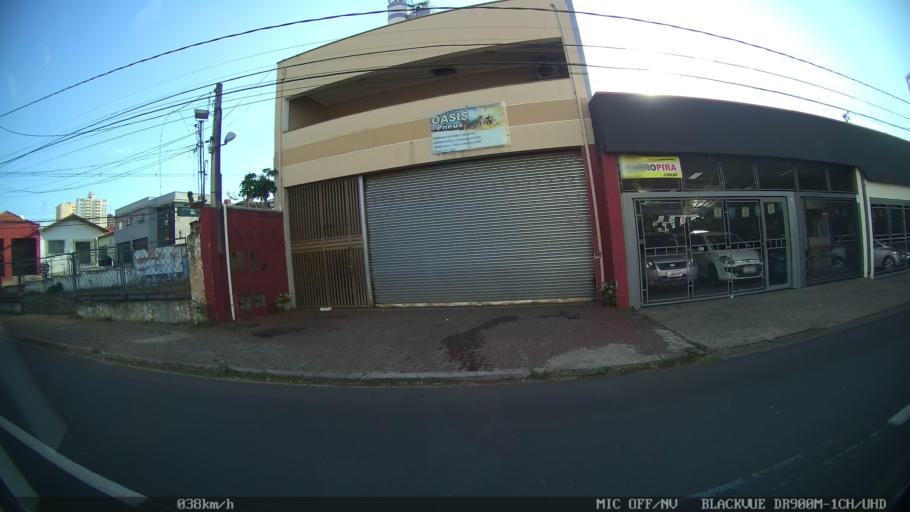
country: BR
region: Sao Paulo
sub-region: Piracicaba
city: Piracicaba
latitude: -22.7174
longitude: -47.6465
